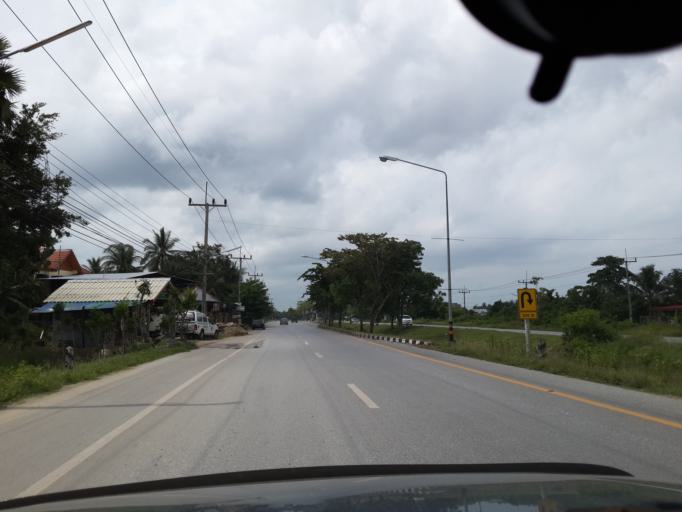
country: TH
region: Pattani
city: Yaring
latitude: 6.8676
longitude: 101.3337
